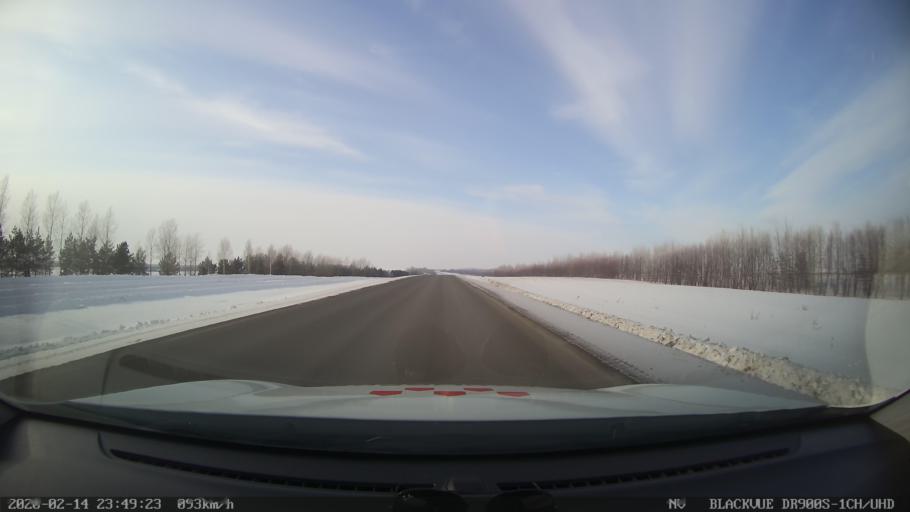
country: RU
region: Tatarstan
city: Kuybyshevskiy Zaton
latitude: 55.2534
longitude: 49.1831
